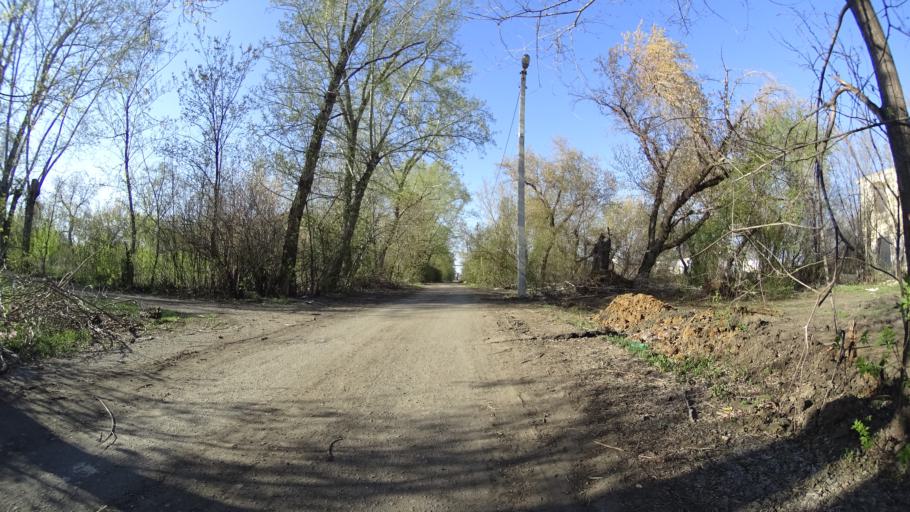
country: RU
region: Chelyabinsk
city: Troitsk
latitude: 54.0994
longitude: 61.5545
